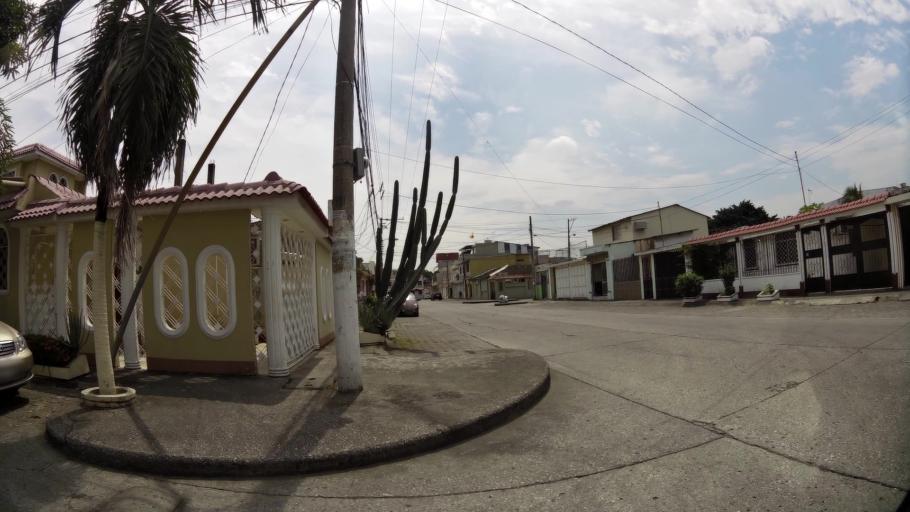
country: EC
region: Guayas
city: Eloy Alfaro
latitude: -2.1361
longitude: -79.9049
